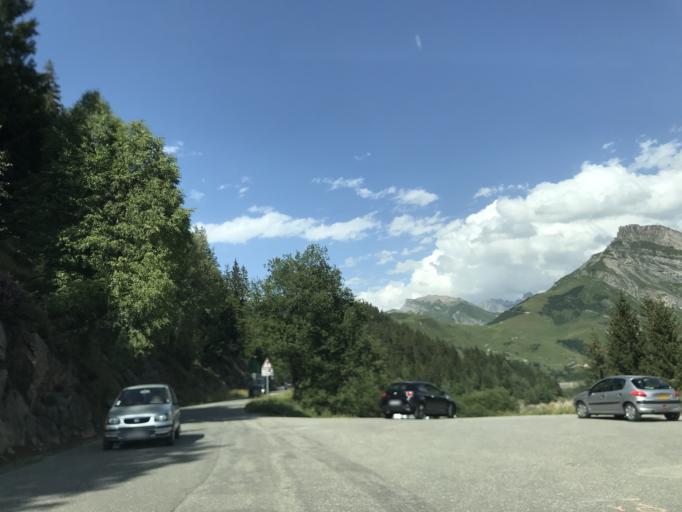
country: FR
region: Rhone-Alpes
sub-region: Departement de la Savoie
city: Beaufort
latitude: 45.6906
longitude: 6.6290
